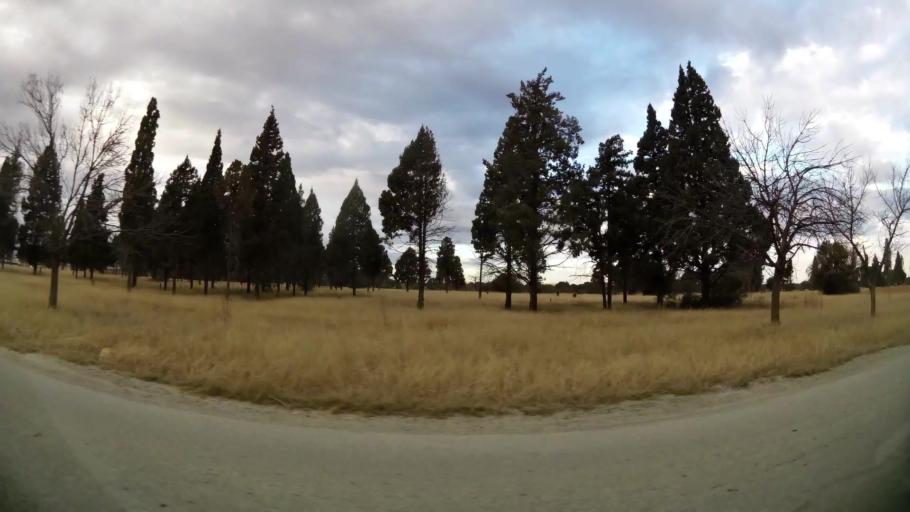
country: ZA
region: Orange Free State
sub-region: Lejweleputswa District Municipality
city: Welkom
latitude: -27.9721
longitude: 26.7006
